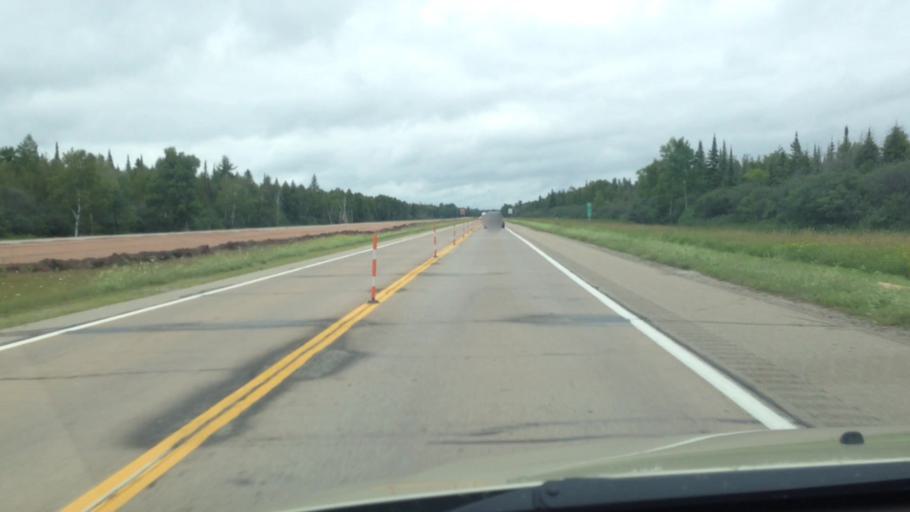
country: US
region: Michigan
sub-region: Delta County
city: Gladstone
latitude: 45.8750
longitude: -87.0173
